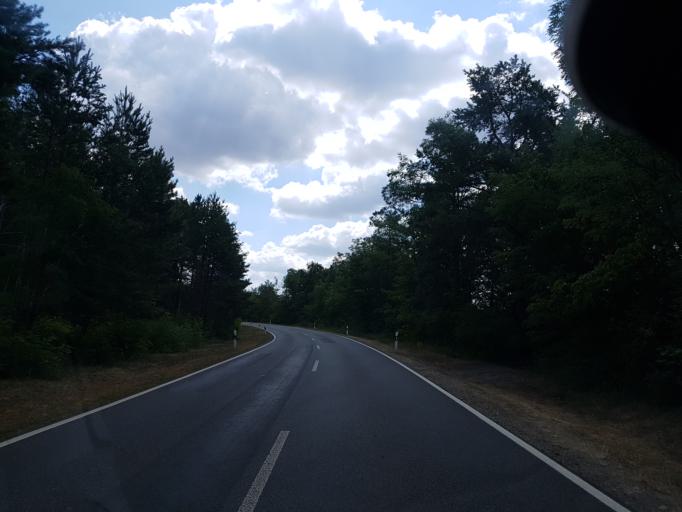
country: DE
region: Brandenburg
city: Neupetershain
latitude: 51.6797
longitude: 14.1551
